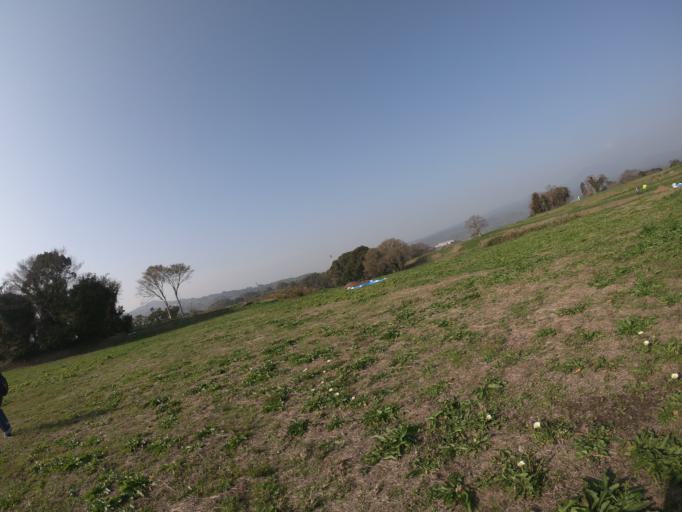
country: JP
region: Nagasaki
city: Shimabara
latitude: 32.6319
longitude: 130.2550
